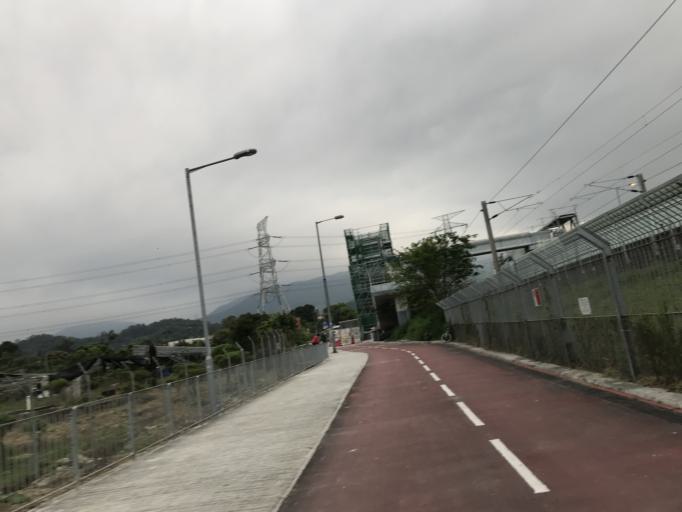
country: HK
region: Tai Po
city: Tai Po
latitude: 22.4693
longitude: 114.1533
